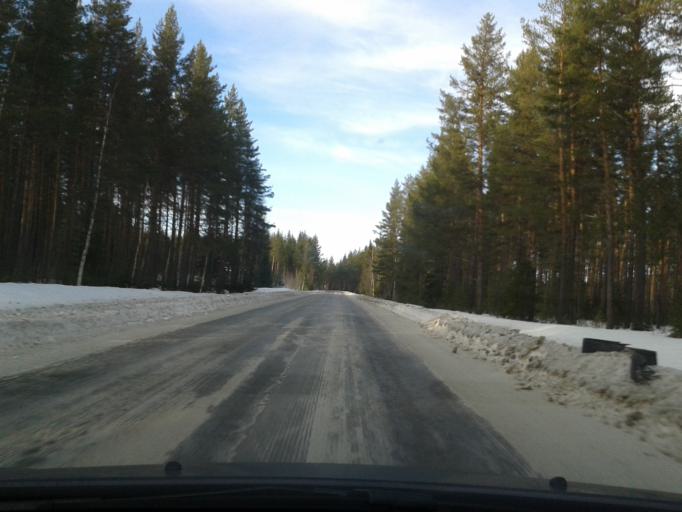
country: SE
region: Vaesternorrland
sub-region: OErnskoeldsviks Kommun
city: Bredbyn
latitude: 63.5468
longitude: 17.9536
